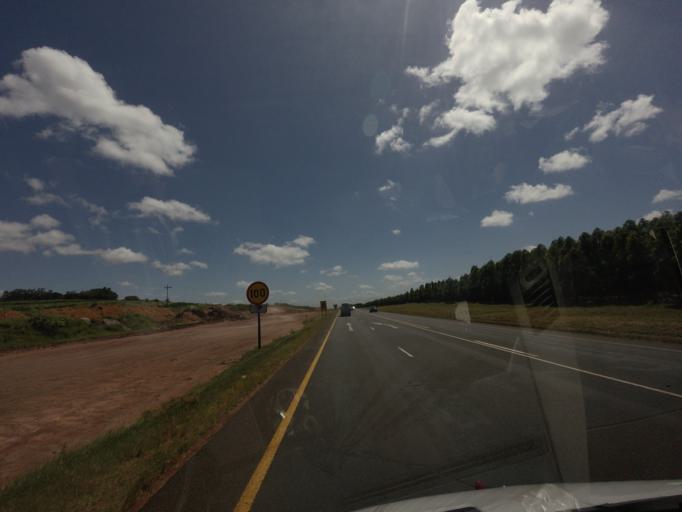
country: ZA
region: KwaZulu-Natal
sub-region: uThungulu District Municipality
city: Empangeni
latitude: -28.8051
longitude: 31.9179
